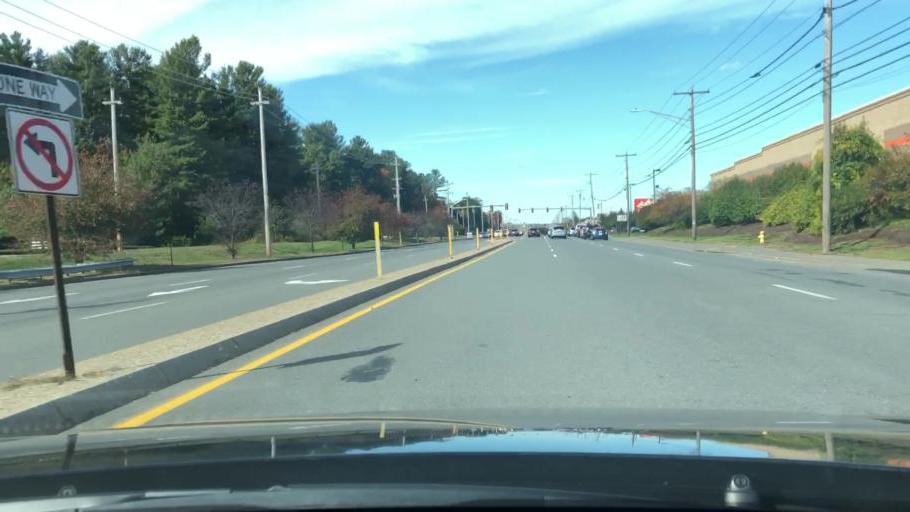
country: US
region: New Hampshire
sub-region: Rockingham County
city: Salem
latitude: 42.7591
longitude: -71.2127
